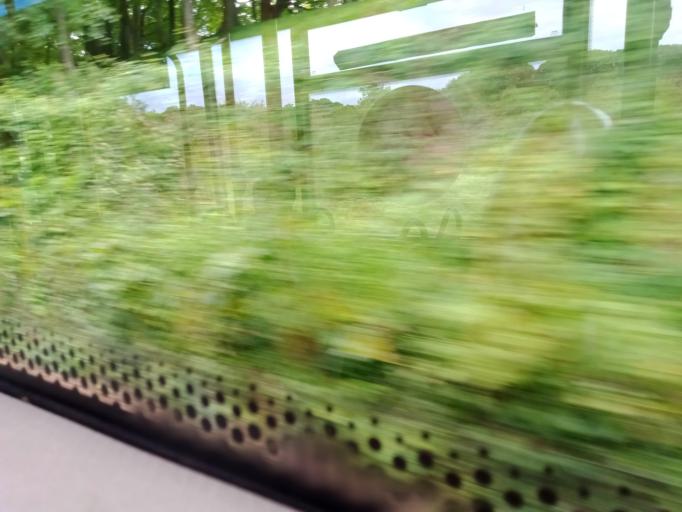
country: GB
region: Wales
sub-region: Anglesey
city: Llangoed
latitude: 53.2907
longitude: -4.0763
